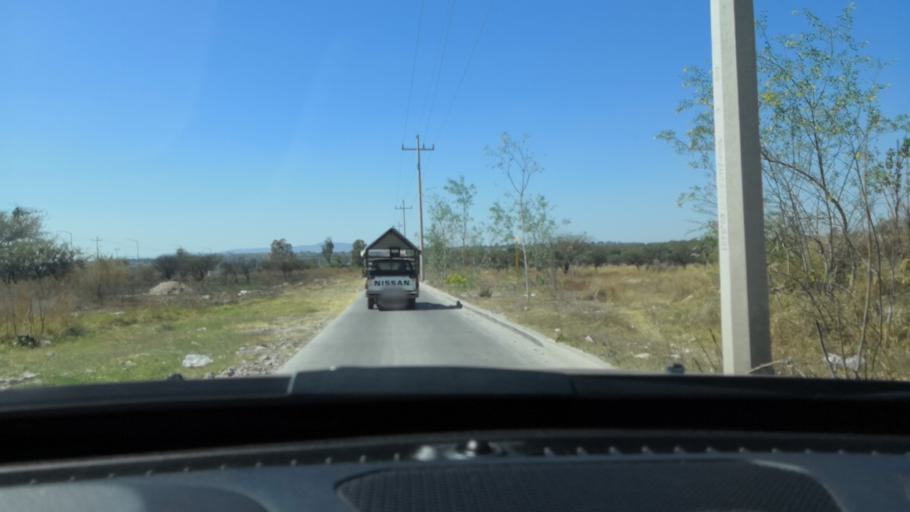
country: MX
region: Guanajuato
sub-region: Leon
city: Centro Familiar la Soledad
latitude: 21.1053
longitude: -101.7678
